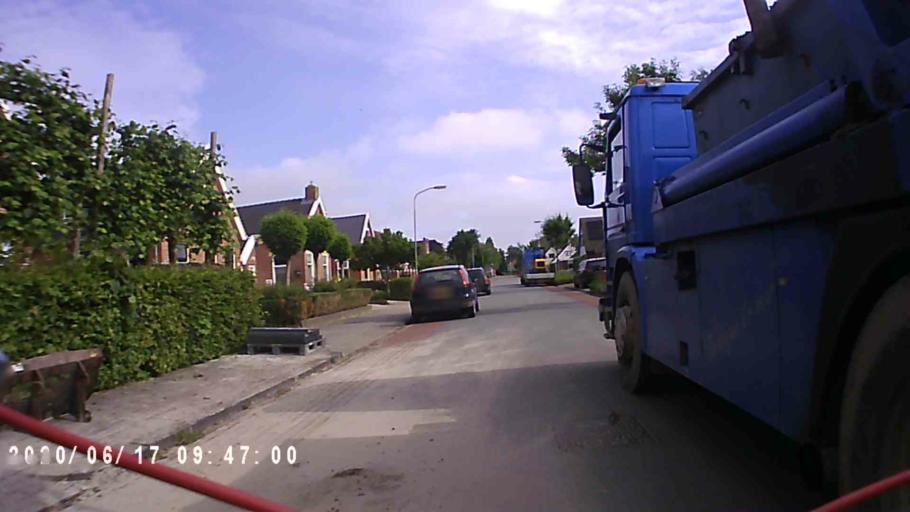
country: NL
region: Groningen
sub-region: Gemeente De Marne
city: Ulrum
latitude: 53.3572
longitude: 6.3382
